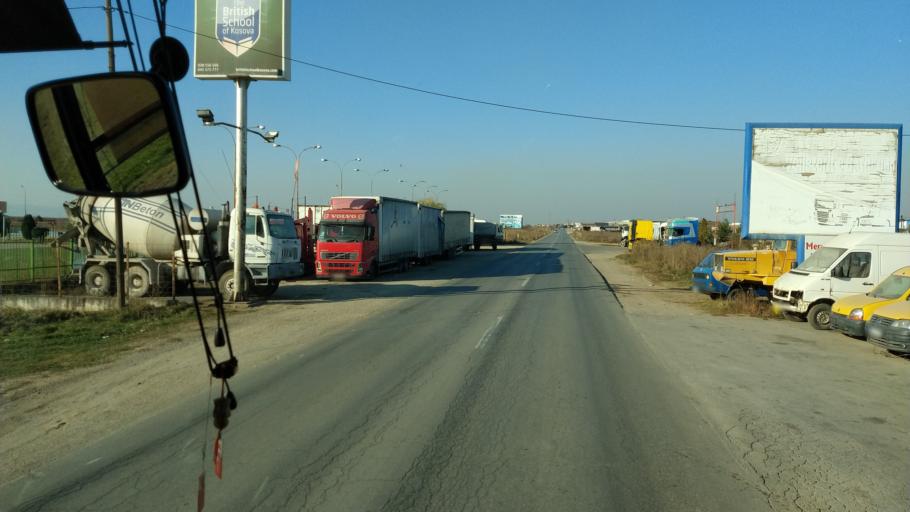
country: XK
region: Pristina
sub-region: Lipjan
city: Lipljan
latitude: 42.5198
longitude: 21.1123
